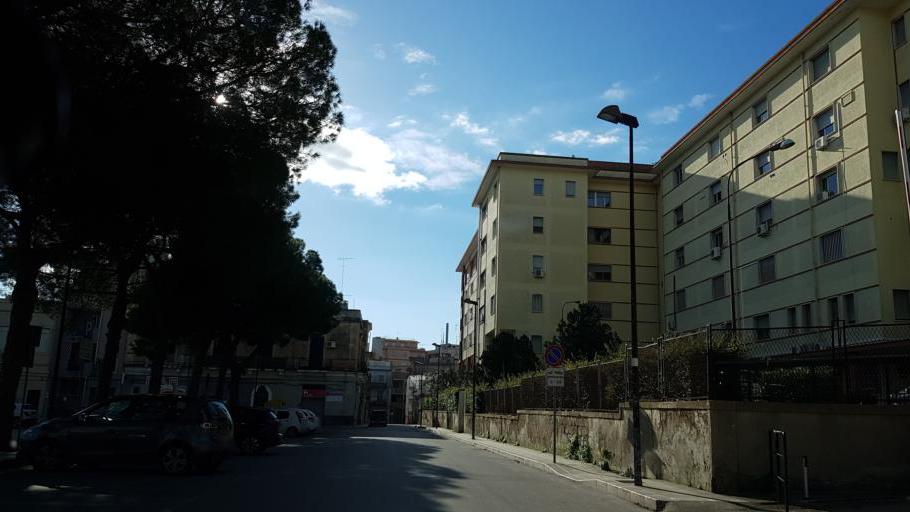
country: IT
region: Apulia
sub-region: Provincia di Brindisi
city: Brindisi
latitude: 40.6359
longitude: 17.9328
